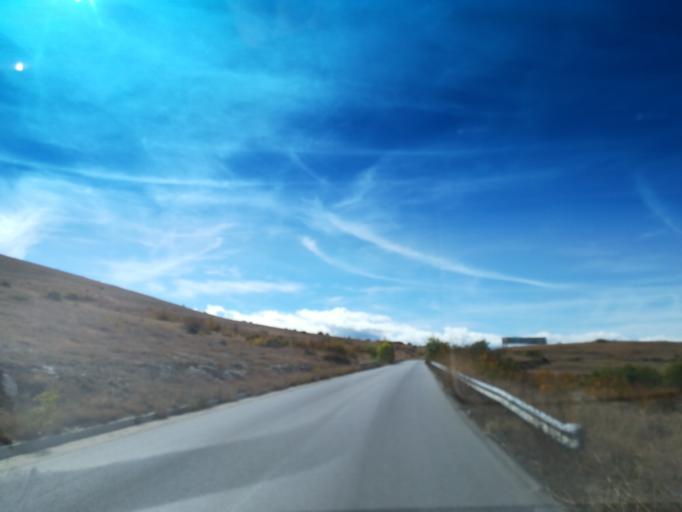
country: BG
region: Plovdiv
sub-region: Obshtina Krichim
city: Krichim
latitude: 42.0986
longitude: 24.4656
